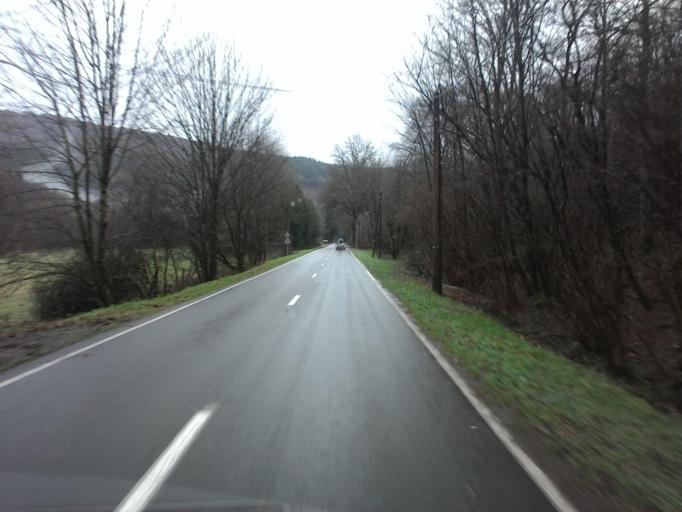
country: BE
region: Wallonia
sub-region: Province de Liege
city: Stoumont
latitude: 50.4115
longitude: 5.7708
